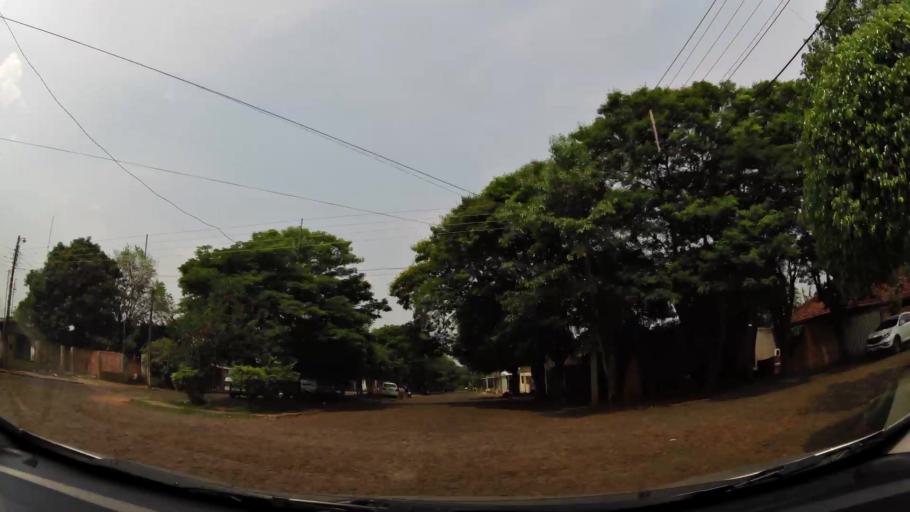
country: PY
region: Alto Parana
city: Presidente Franco
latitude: -25.5458
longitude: -54.6274
